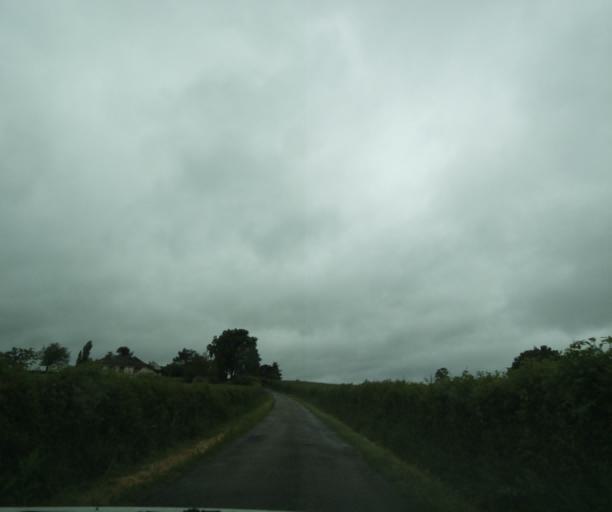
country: FR
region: Bourgogne
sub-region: Departement de Saone-et-Loire
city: Genelard
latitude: 46.5754
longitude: 4.2166
